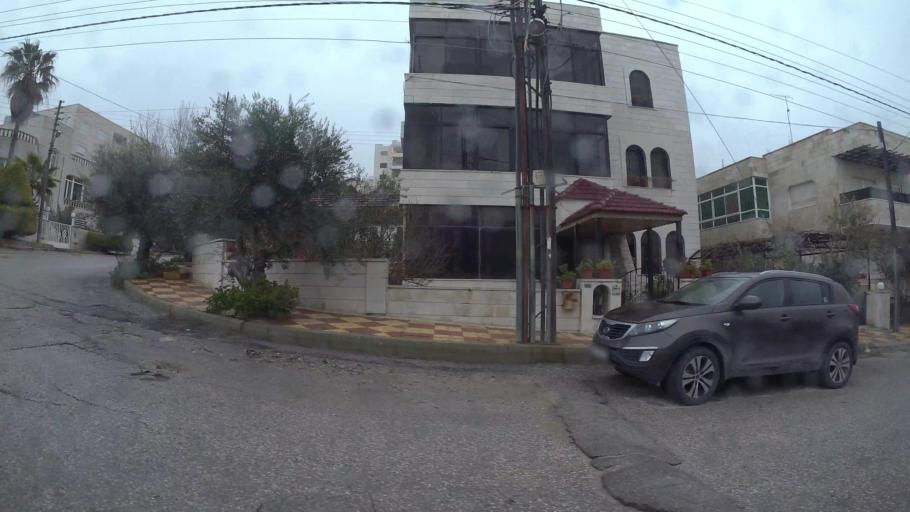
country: JO
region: Amman
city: Al Jubayhah
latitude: 32.0357
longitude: 35.8534
